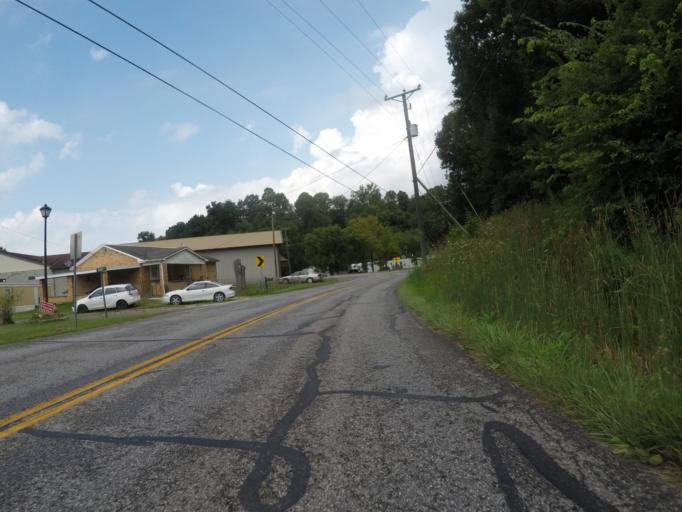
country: US
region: Kentucky
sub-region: Boyd County
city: Meads
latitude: 38.4179
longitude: -82.6977
